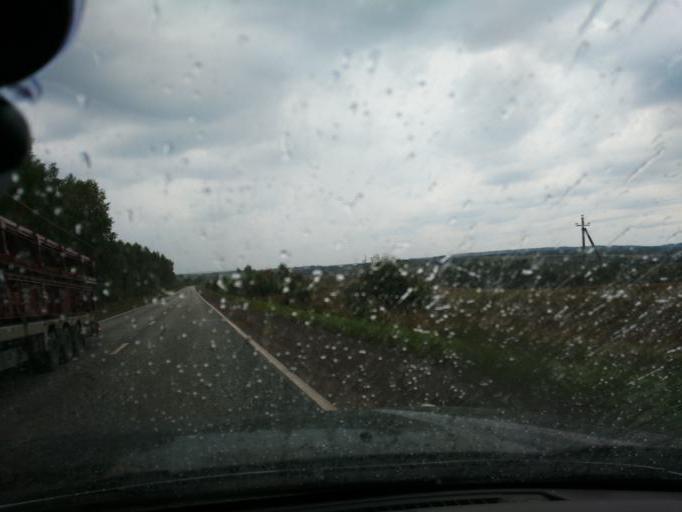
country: RU
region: Perm
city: Chernushka
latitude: 56.8476
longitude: 55.9586
